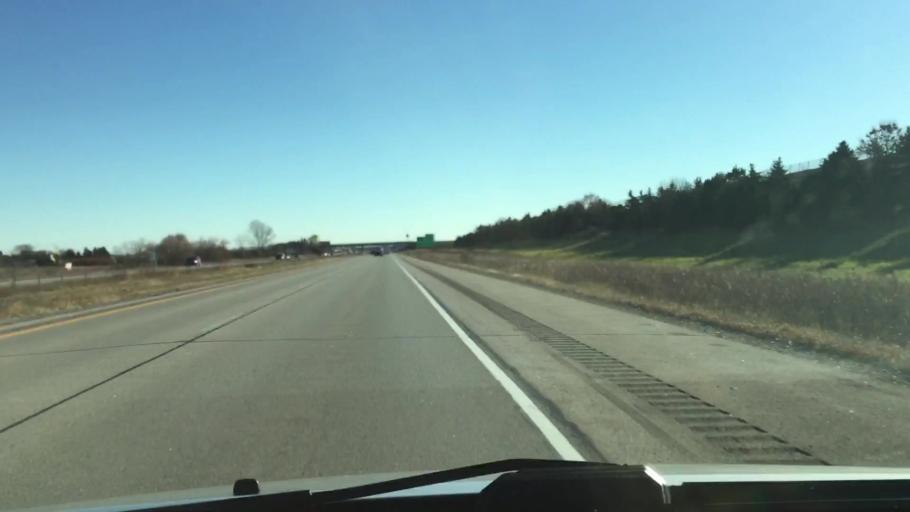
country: US
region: Wisconsin
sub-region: Outagamie County
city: Kimberly
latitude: 44.2979
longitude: -88.3407
